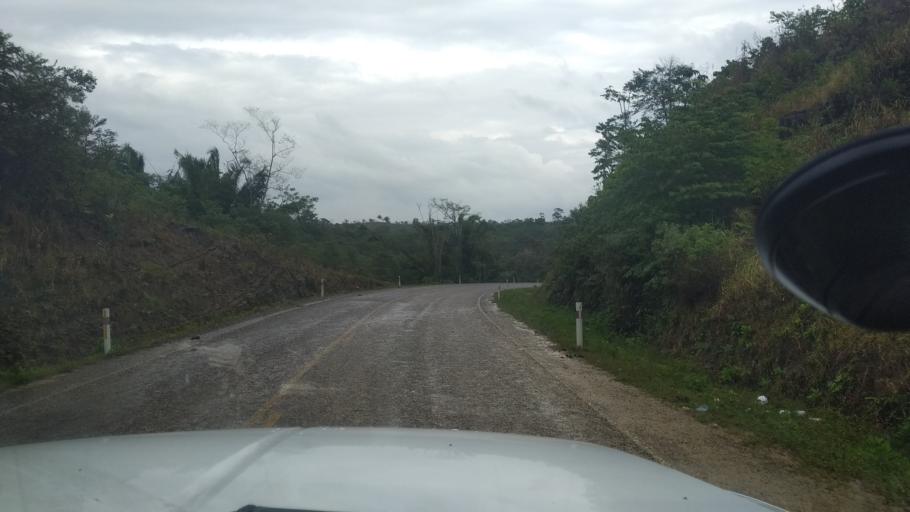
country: GT
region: Peten
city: San Luis
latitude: 16.1844
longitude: -89.2071
